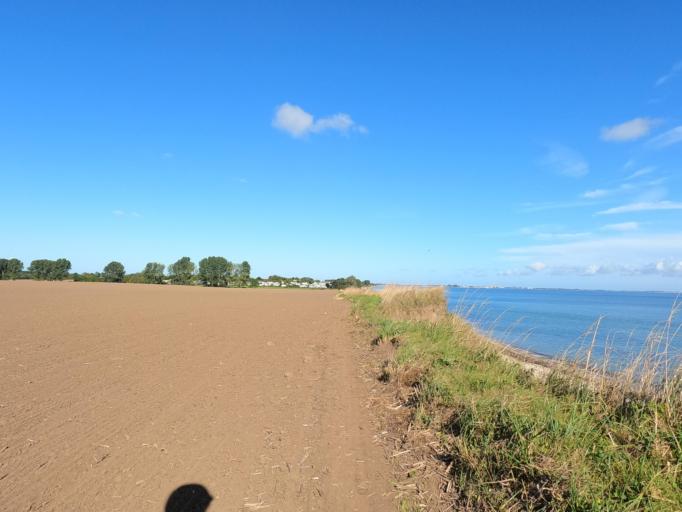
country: DE
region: Schleswig-Holstein
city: Neukirchen
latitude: 54.2982
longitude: 11.0772
